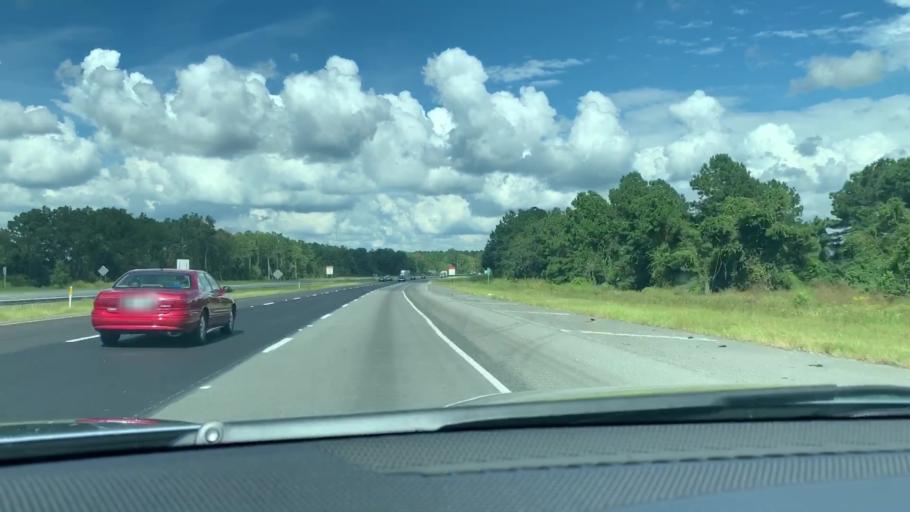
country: US
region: Georgia
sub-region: Camden County
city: Woodbine
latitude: 31.0397
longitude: -81.6523
